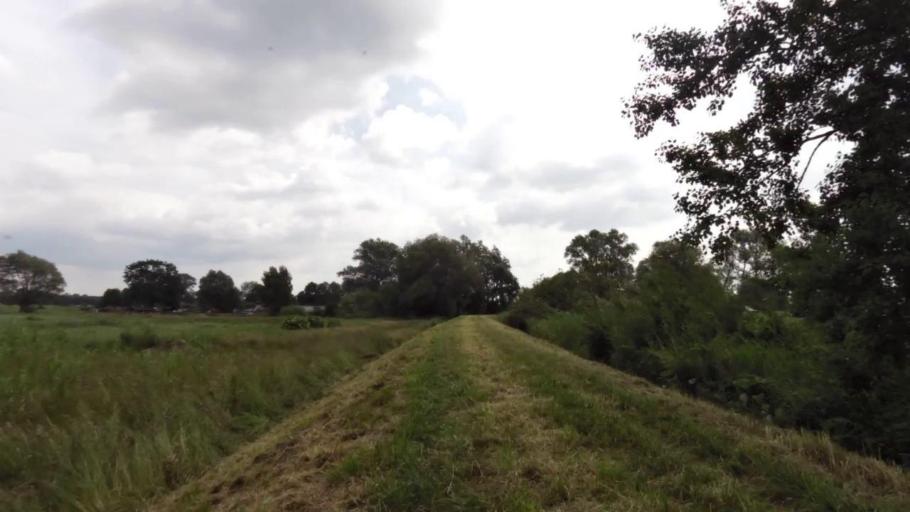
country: PL
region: West Pomeranian Voivodeship
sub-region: Powiat policki
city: Police
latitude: 53.5090
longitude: 14.6978
